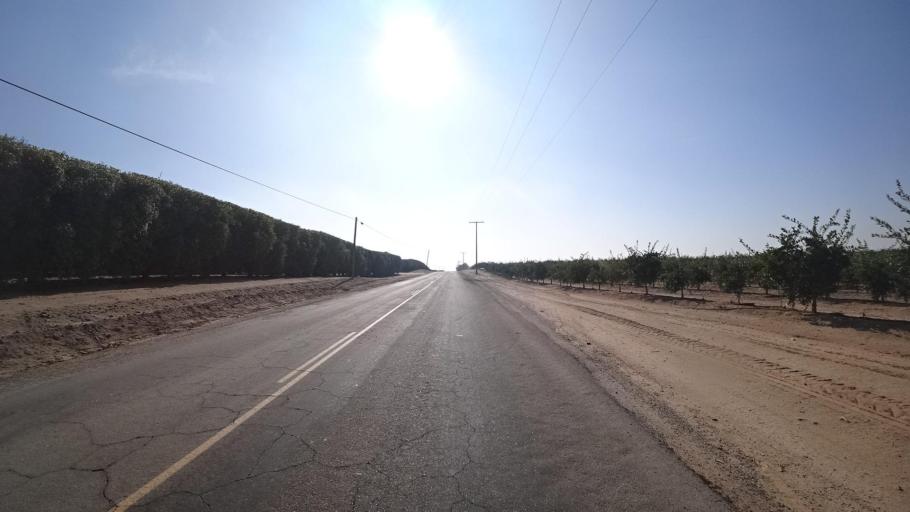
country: US
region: California
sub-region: Kern County
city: McFarland
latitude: 35.6681
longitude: -119.1340
